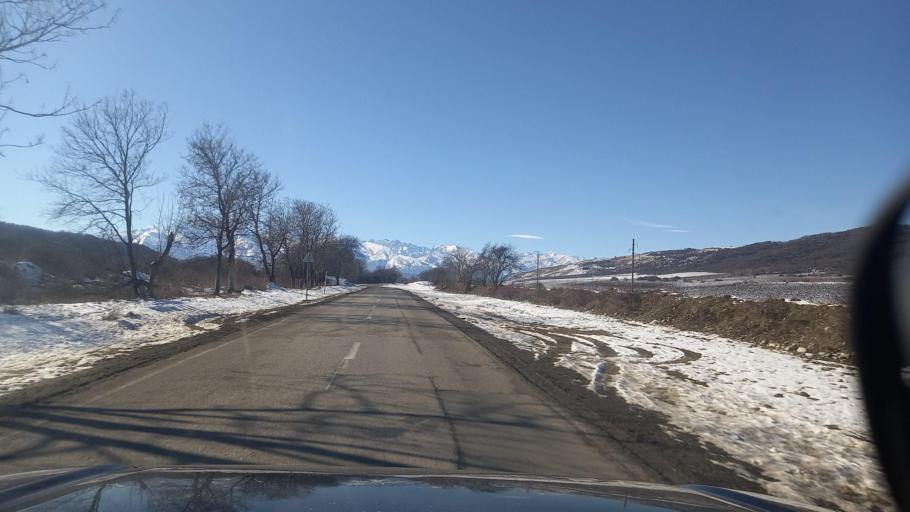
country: RU
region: North Ossetia
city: Chikola
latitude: 43.2459
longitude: 43.9616
